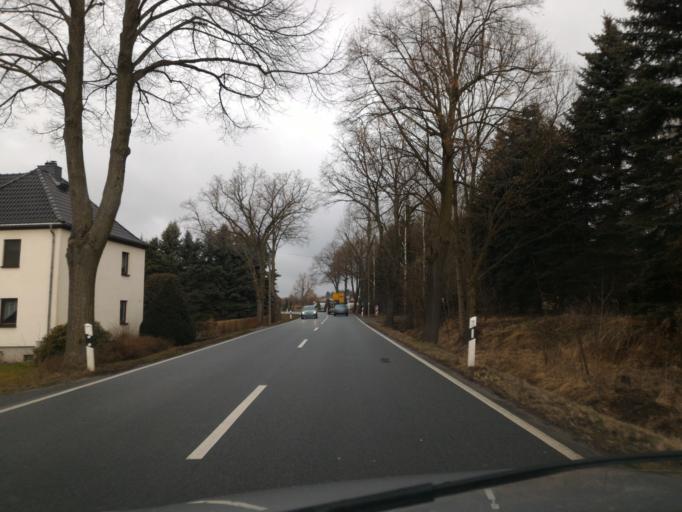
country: DE
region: Saxony
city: Neugersdorf
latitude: 50.9779
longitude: 14.6340
